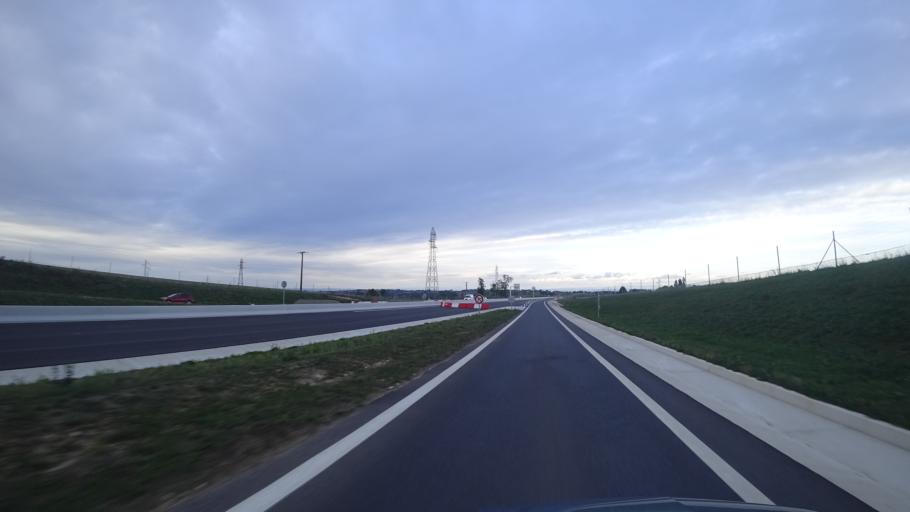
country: FR
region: Midi-Pyrenees
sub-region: Departement de l'Aveyron
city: Baraqueville
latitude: 44.2847
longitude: 2.4284
